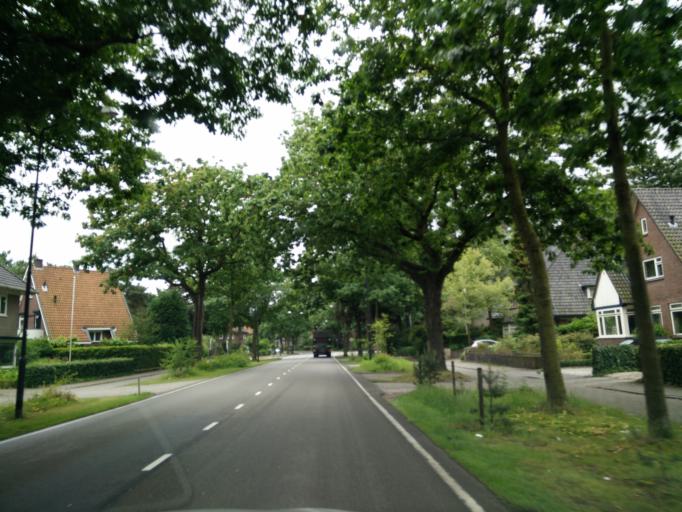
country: NL
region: Gelderland
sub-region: Gemeente Apeldoorn
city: Apeldoorn
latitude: 52.2167
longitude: 5.9341
